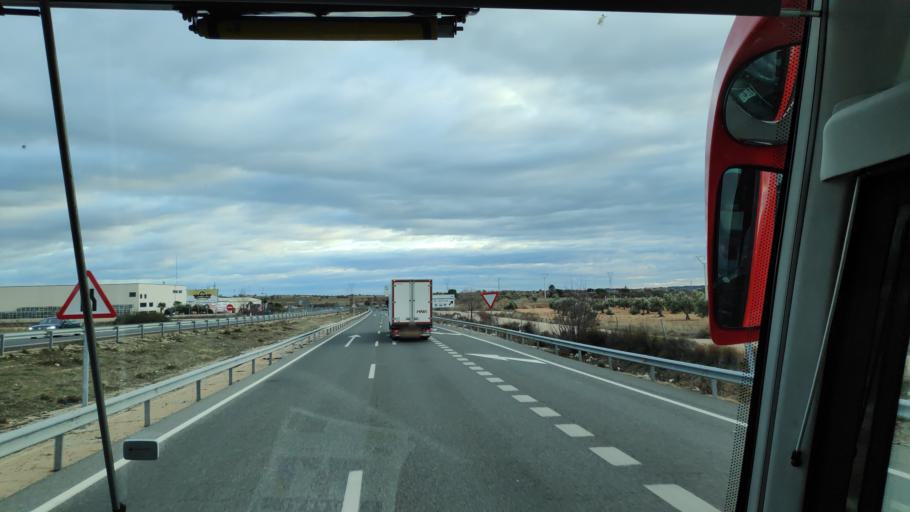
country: ES
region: Madrid
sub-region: Provincia de Madrid
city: Villarejo de Salvanes
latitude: 40.1781
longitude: -3.2963
